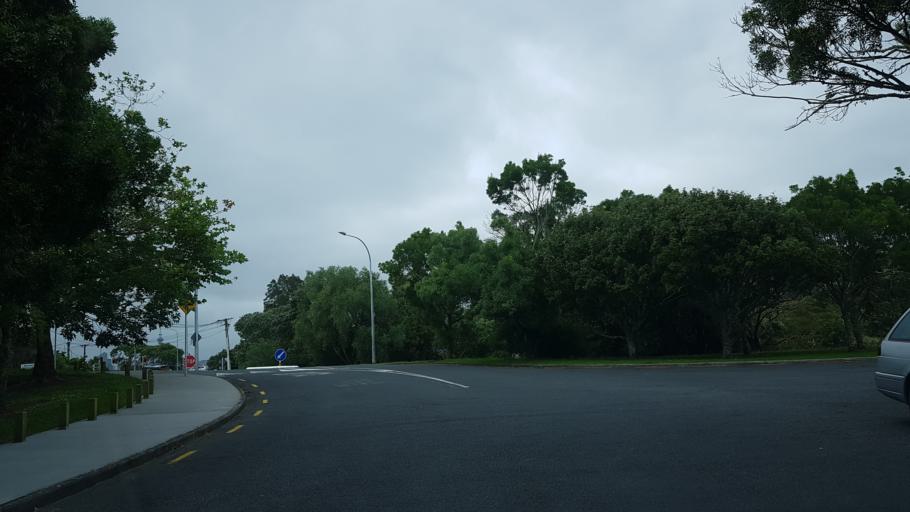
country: NZ
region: Auckland
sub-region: Auckland
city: North Shore
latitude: -36.8108
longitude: 174.7502
